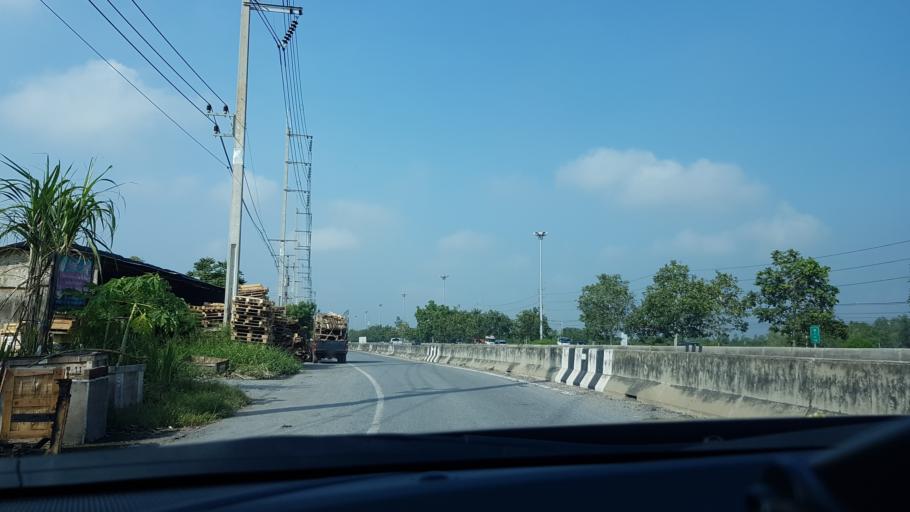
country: TH
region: Phra Nakhon Si Ayutthaya
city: Bang Pa-in
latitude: 14.1550
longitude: 100.5656
